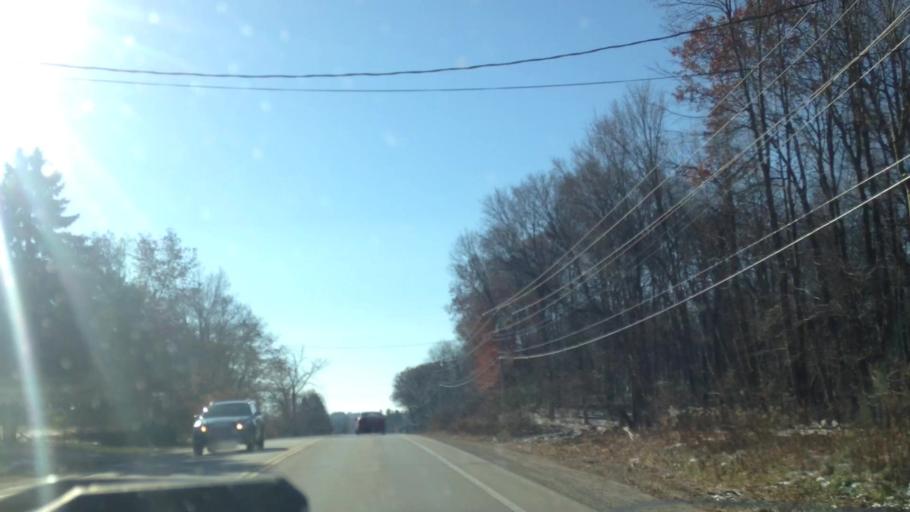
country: US
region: Wisconsin
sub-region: Washington County
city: West Bend
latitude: 43.4032
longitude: -88.1612
